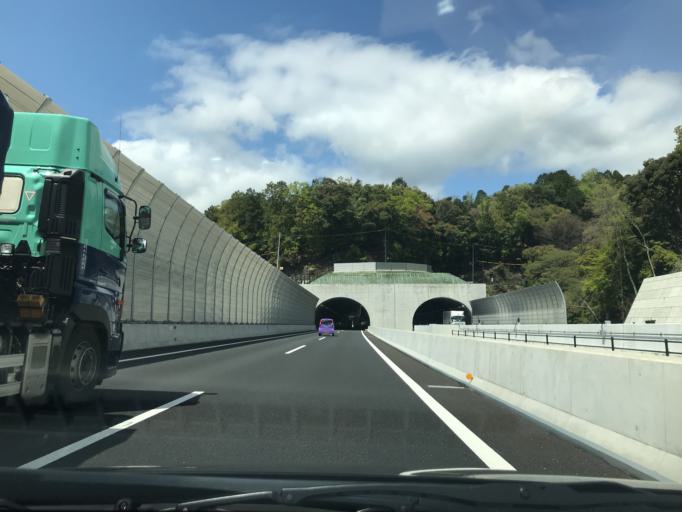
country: JP
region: Osaka
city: Takatsuki
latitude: 34.8933
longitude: 135.6083
